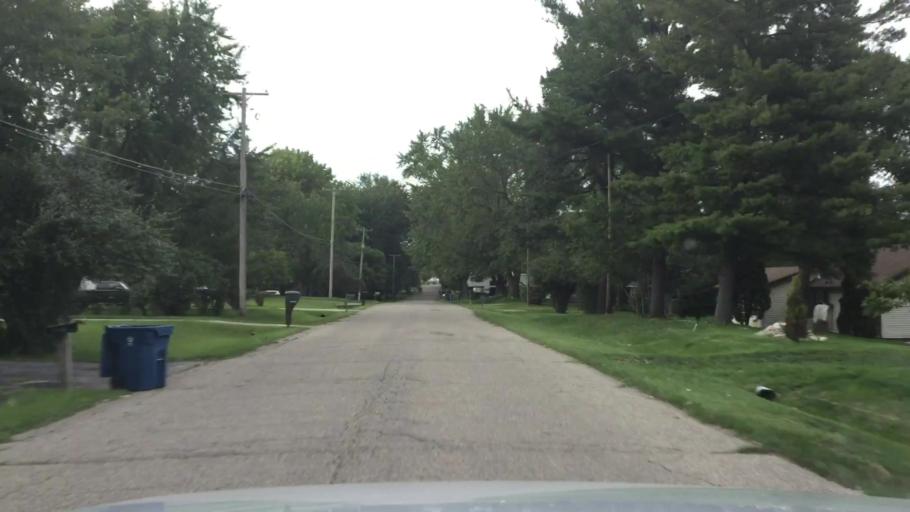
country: US
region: Michigan
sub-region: Genesee County
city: Linden
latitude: 42.8078
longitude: -83.7994
